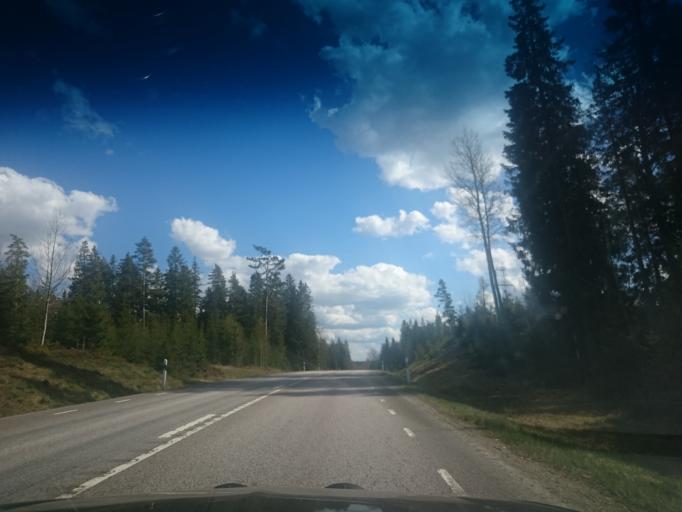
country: SE
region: Kronoberg
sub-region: Vaxjo Kommun
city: Braas
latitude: 57.2414
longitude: 15.1420
